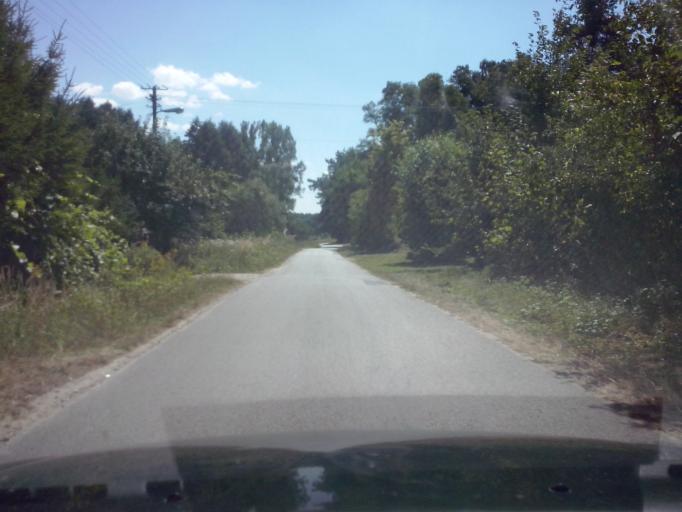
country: PL
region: Swietokrzyskie
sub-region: Powiat buski
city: Gnojno
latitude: 50.6172
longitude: 20.8855
